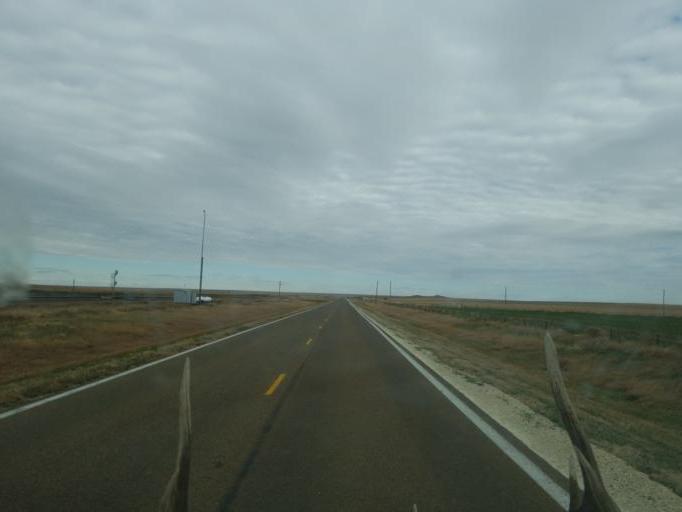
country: US
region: Kansas
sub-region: Wallace County
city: Sharon Springs
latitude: 38.9937
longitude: -101.4082
